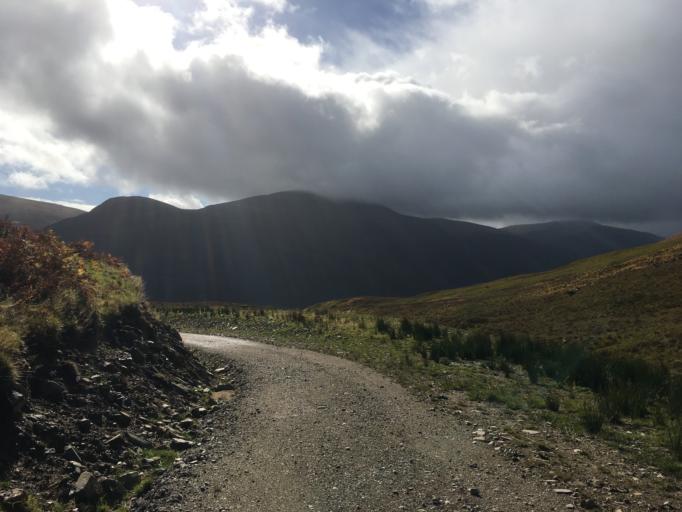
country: GB
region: Scotland
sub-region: Highland
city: Spean Bridge
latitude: 57.3486
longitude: -4.9828
